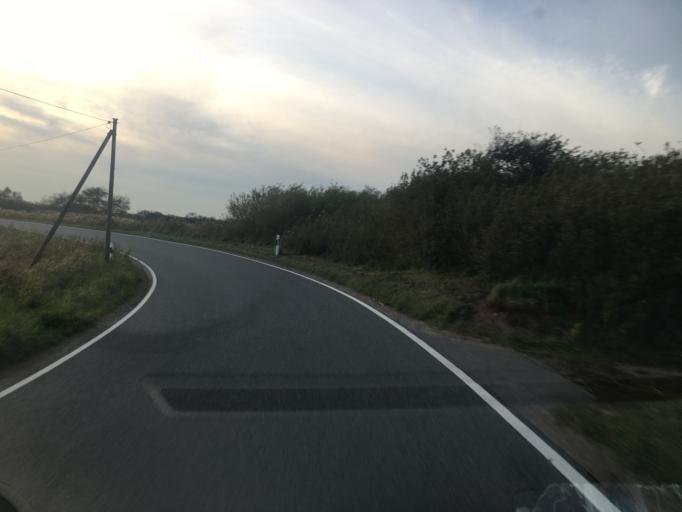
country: DE
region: Schleswig-Holstein
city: Aventoft
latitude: 54.9050
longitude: 8.8374
